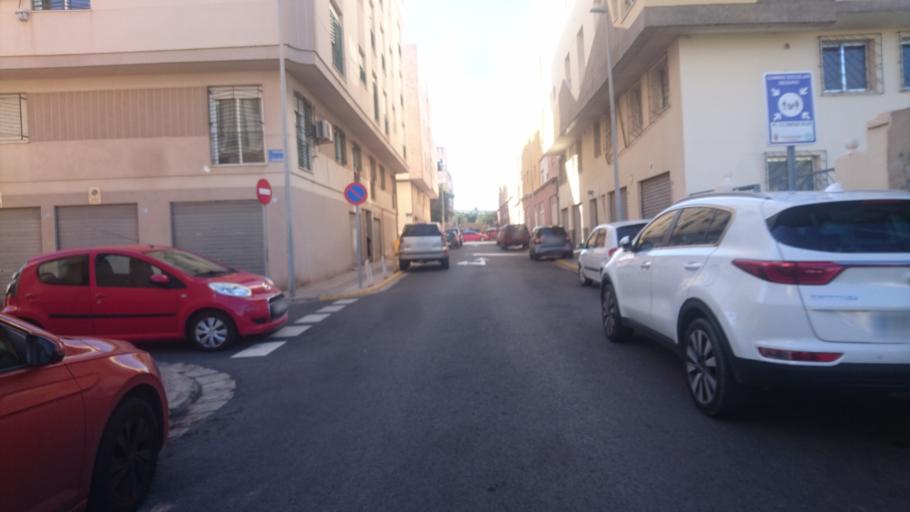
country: ES
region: Melilla
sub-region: Melilla
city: Melilla
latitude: 35.2762
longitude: -2.9453
